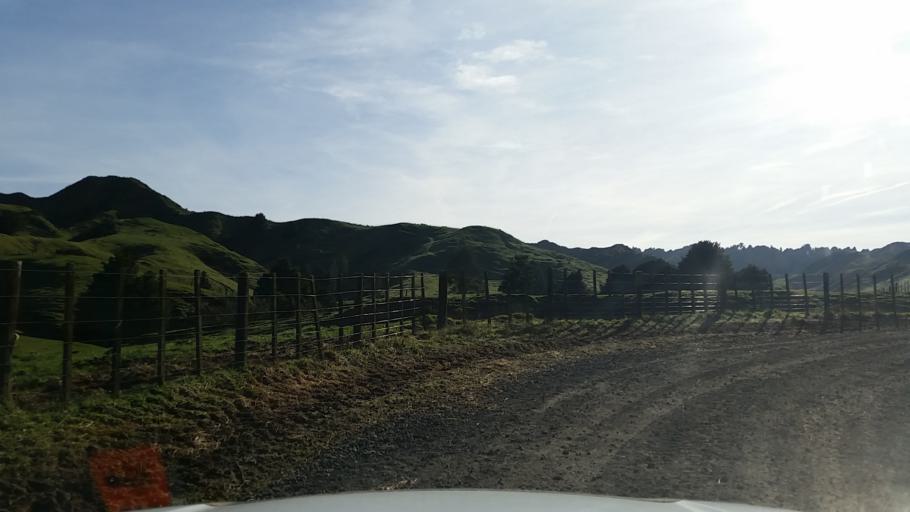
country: NZ
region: Taranaki
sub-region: South Taranaki District
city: Eltham
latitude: -39.3148
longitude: 174.5342
